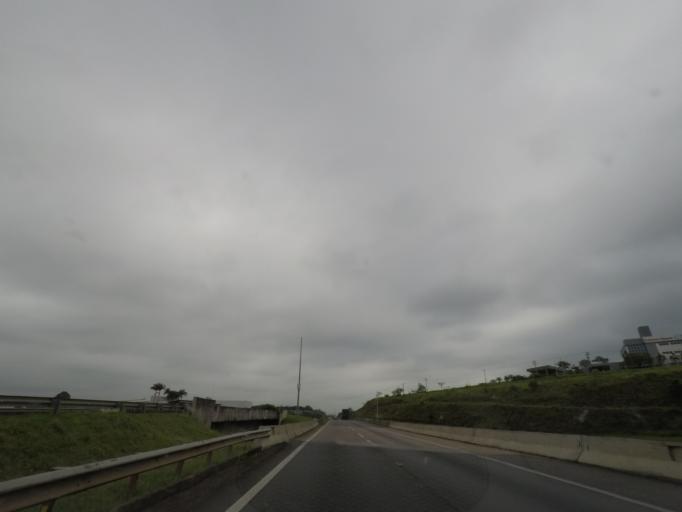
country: BR
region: Sao Paulo
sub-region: Itatiba
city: Itatiba
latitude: -22.9925
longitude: -46.7948
